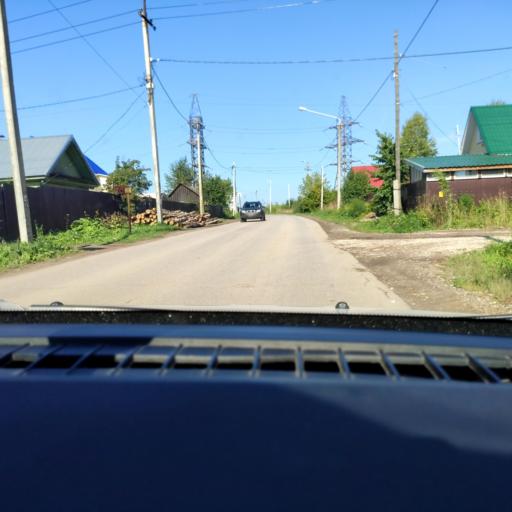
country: RU
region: Perm
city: Novyye Lyady
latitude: 58.0533
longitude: 56.5962
